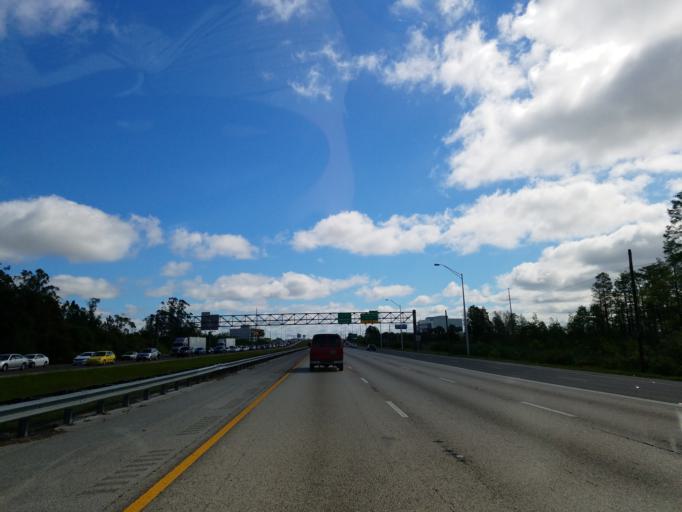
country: US
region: Florida
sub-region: Orange County
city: Oak Ridge
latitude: 28.4817
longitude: -81.4456
